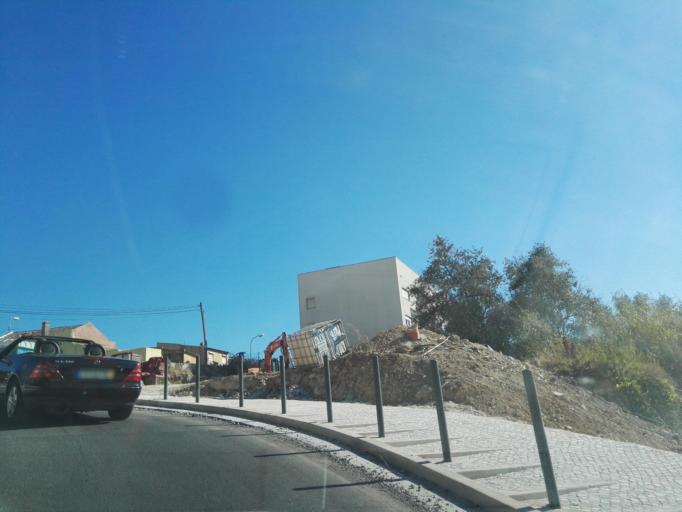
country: PT
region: Lisbon
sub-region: Lisbon
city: Lisbon
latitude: 38.7248
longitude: -9.1678
